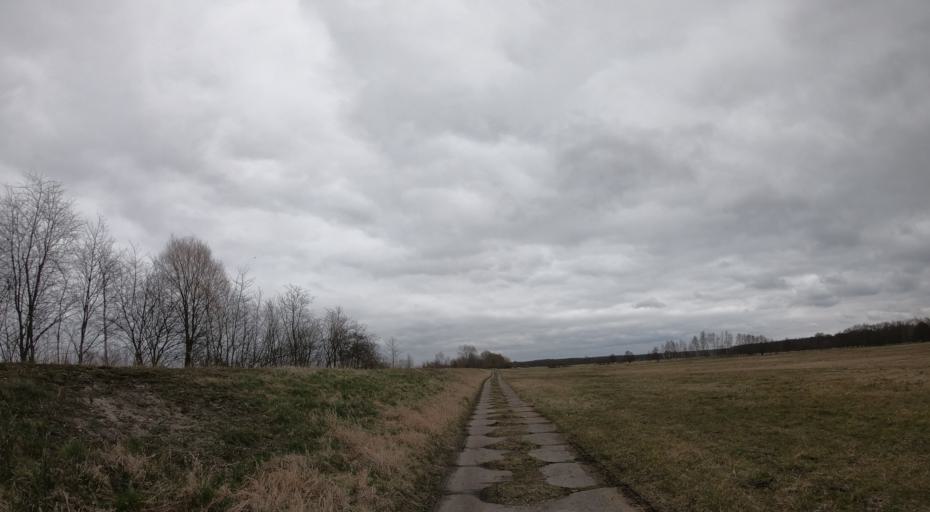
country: PL
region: West Pomeranian Voivodeship
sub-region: Powiat policki
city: Nowe Warpno
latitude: 53.6931
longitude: 14.3798
